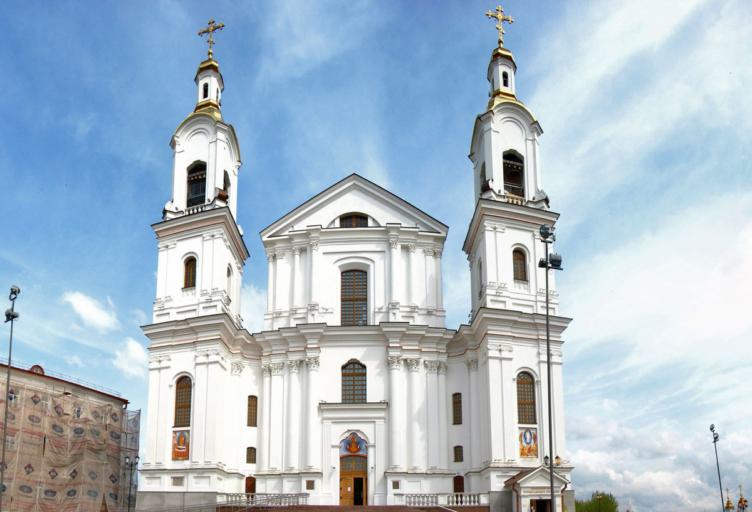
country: BY
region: Vitebsk
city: Vitebsk
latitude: 55.1958
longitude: 30.2018
